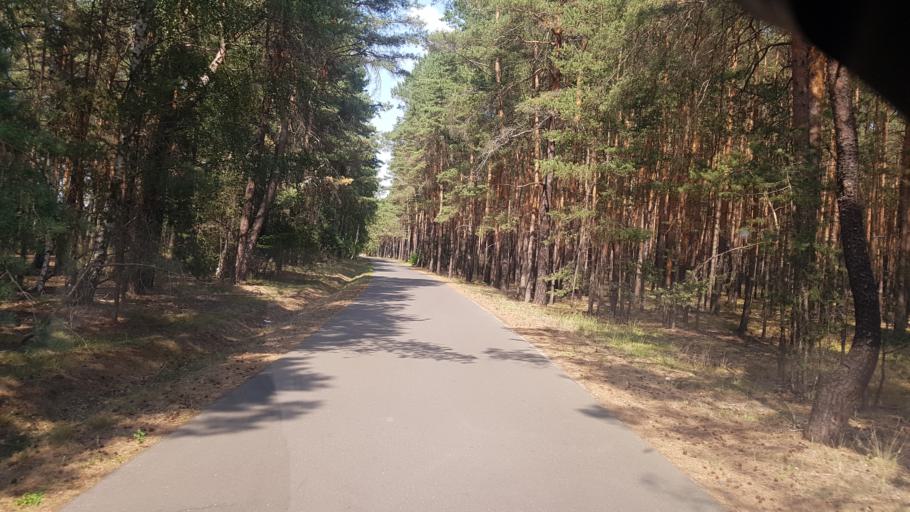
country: DE
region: Brandenburg
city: Spremberg
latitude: 51.6224
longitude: 14.4011
